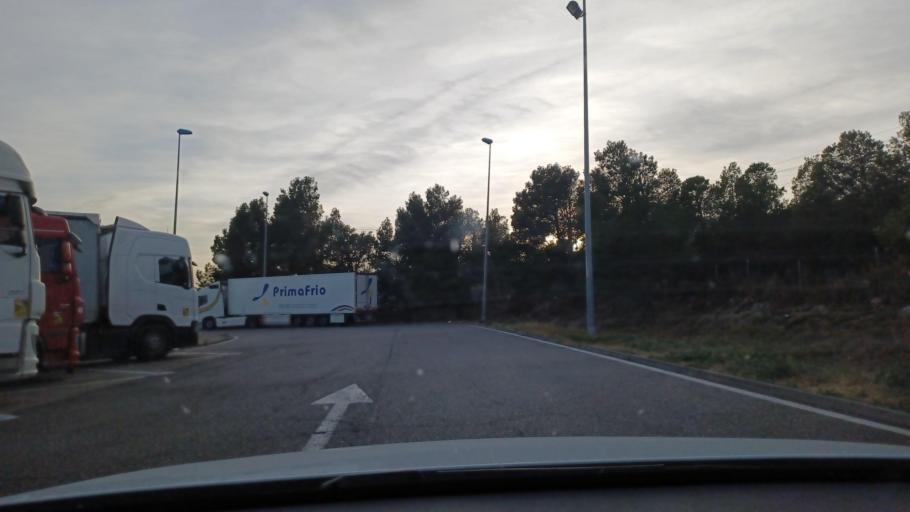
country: ES
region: Catalonia
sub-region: Provincia de Tarragona
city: Colldejou
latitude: 40.9869
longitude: 0.8938
